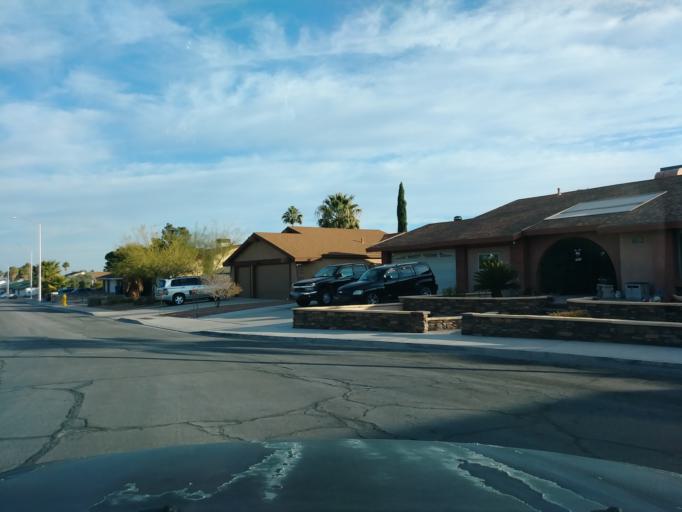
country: US
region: Nevada
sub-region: Clark County
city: Spring Valley
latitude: 36.1717
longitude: -115.2413
